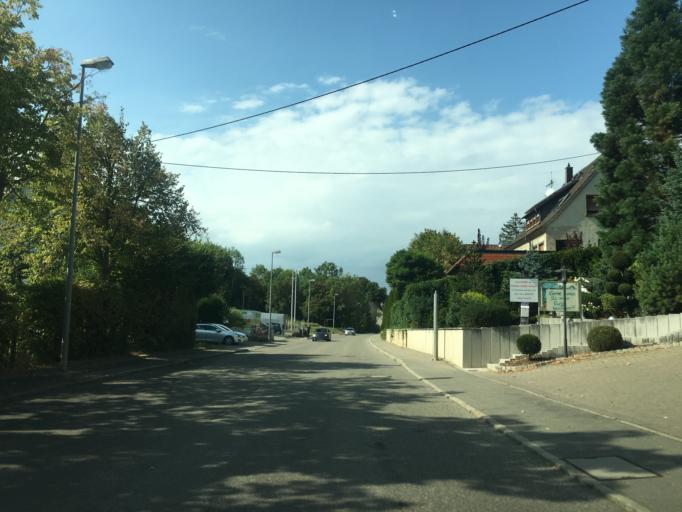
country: DE
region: Baden-Wuerttemberg
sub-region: Tuebingen Region
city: Gomaringen
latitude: 48.4284
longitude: 9.1612
